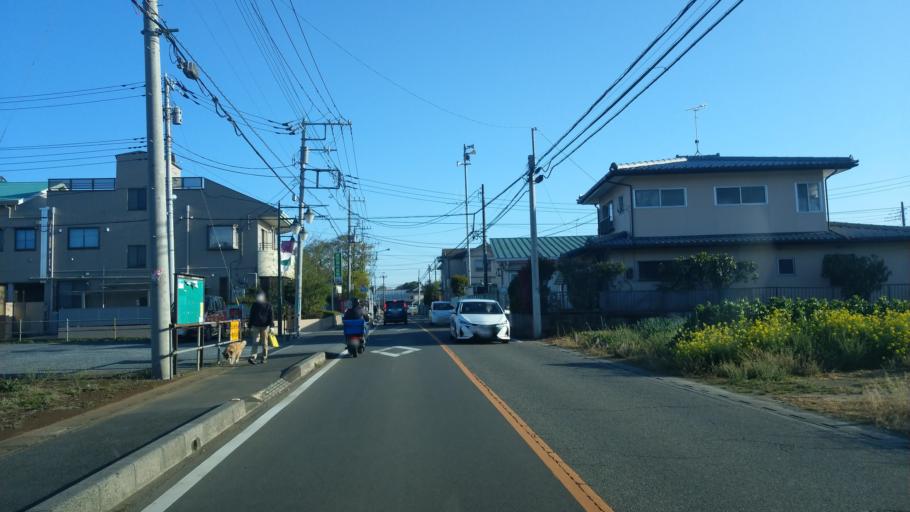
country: JP
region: Saitama
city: Ageoshimo
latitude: 35.9279
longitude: 139.5711
